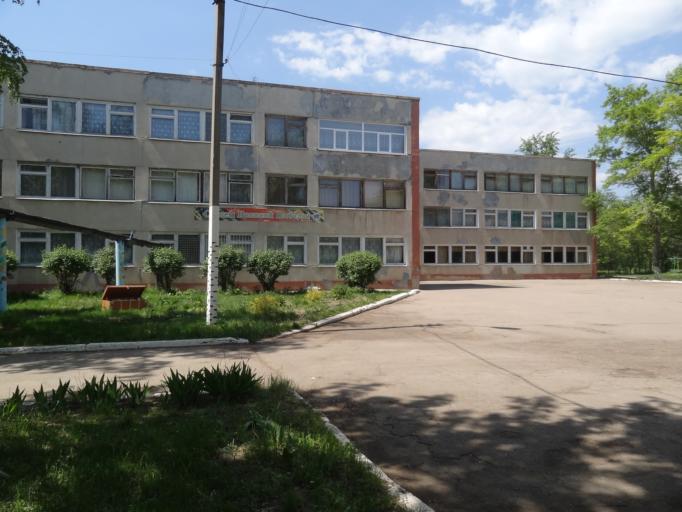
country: RU
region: Saratov
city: Privolzhskiy
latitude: 51.3916
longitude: 46.1206
